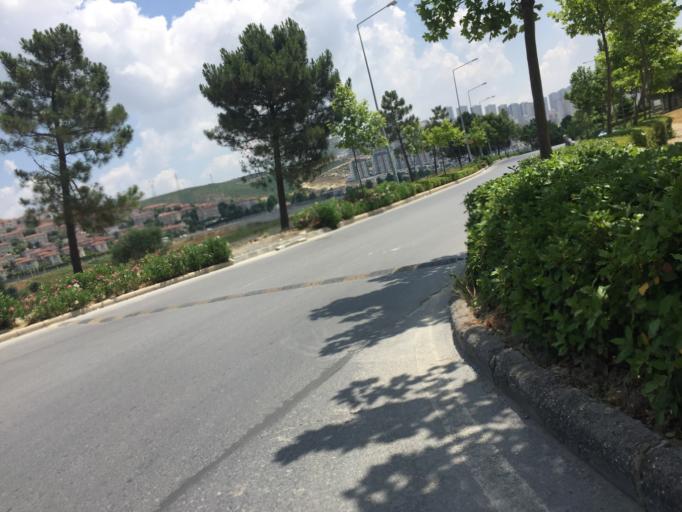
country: TR
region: Istanbul
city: Esenyurt
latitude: 41.0860
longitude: 28.6718
